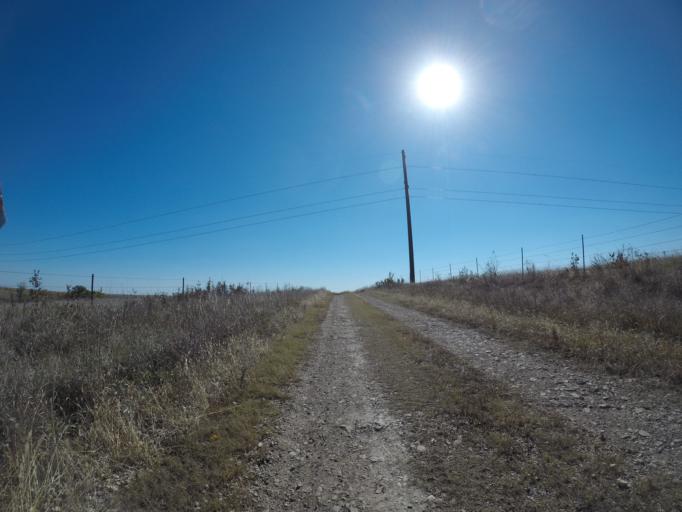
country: US
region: Kansas
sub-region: Wabaunsee County
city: Alma
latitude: 38.9952
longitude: -96.4642
